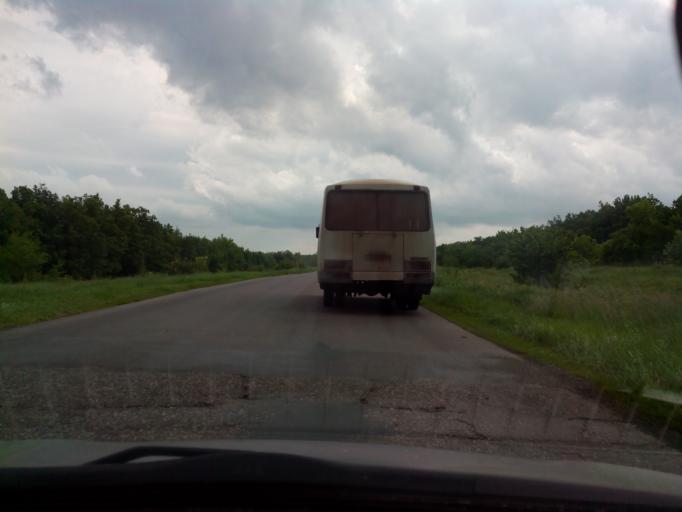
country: RU
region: Volgograd
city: Mikhaylovka
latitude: 49.9674
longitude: 43.0423
